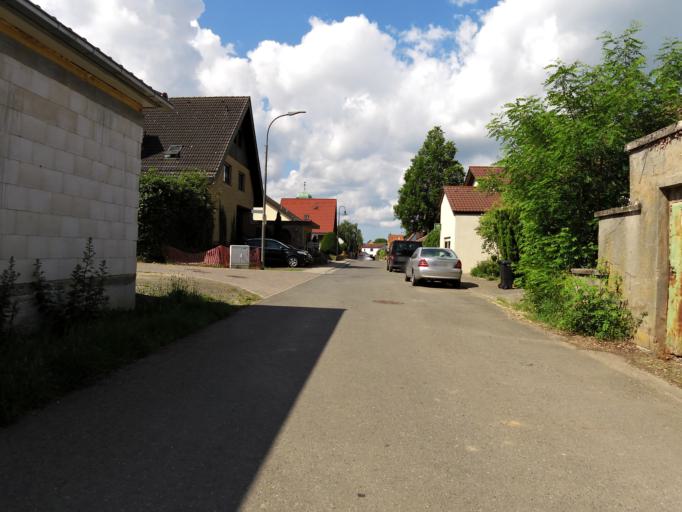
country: DE
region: Rheinland-Pfalz
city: Tiefenthal
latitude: 49.5416
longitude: 8.1087
